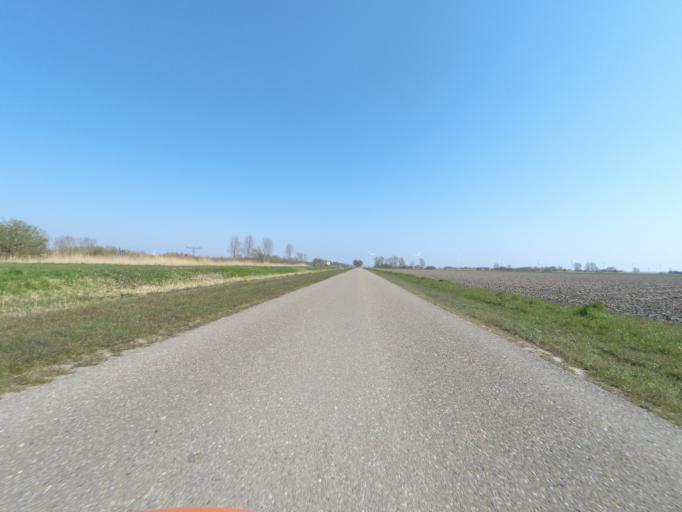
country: NL
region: Utrecht
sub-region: Gemeente Bunschoten
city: Spakenburg
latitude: 52.3080
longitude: 5.3500
